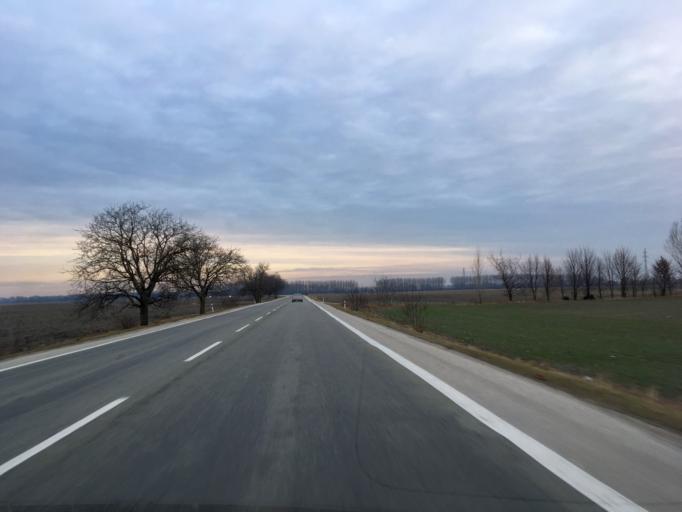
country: SK
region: Trnavsky
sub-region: Okres Dunajska Streda
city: Velky Meder
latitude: 47.9191
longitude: 17.7265
